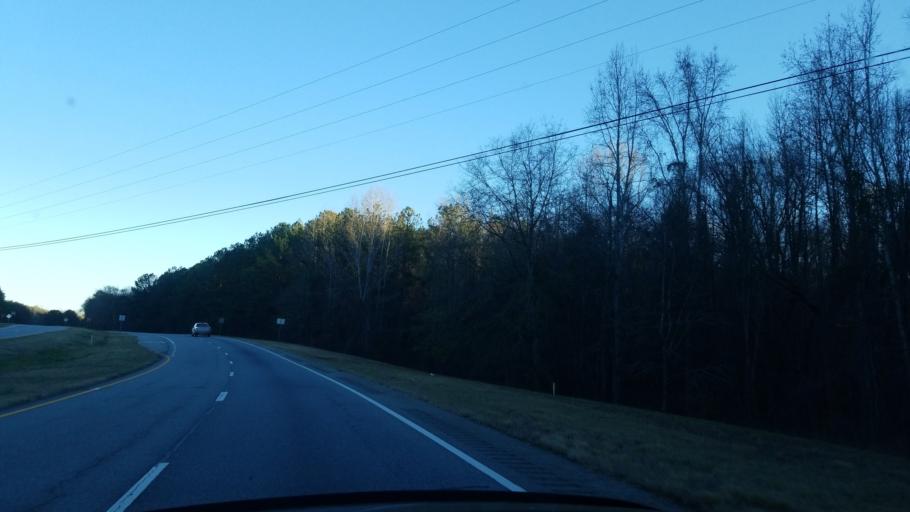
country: US
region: Georgia
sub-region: Chattahoochee County
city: Cusseta
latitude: 32.2645
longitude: -84.7402
